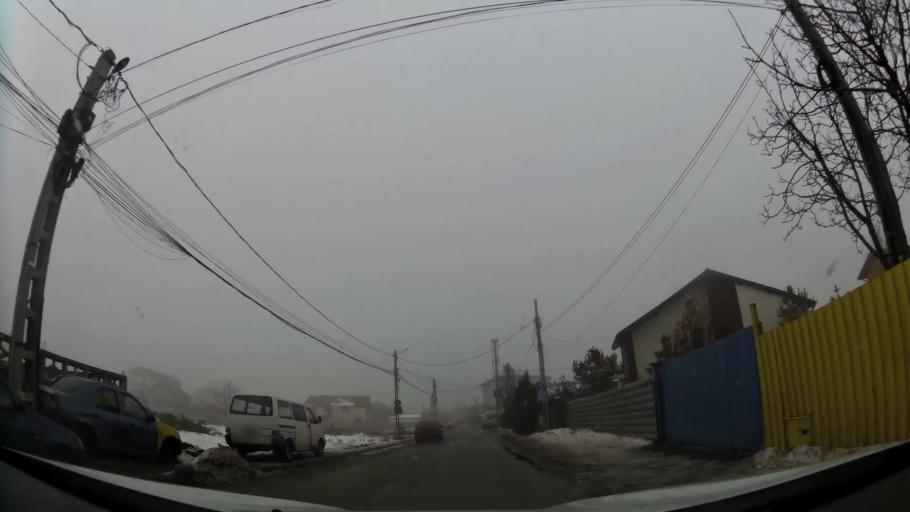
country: RO
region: Ilfov
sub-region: Comuna Chiajna
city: Chiajna
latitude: 44.4553
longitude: 25.9824
